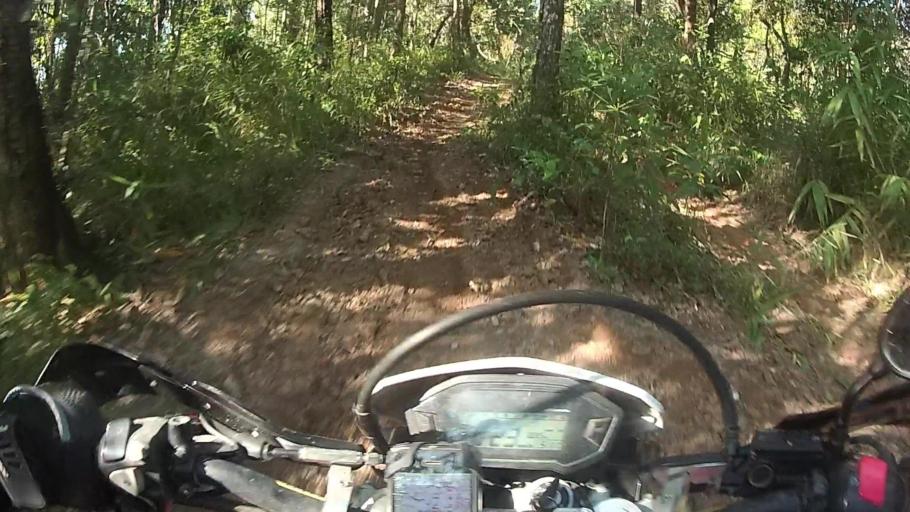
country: TH
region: Chiang Mai
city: Phrao
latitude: 19.4146
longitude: 99.2951
